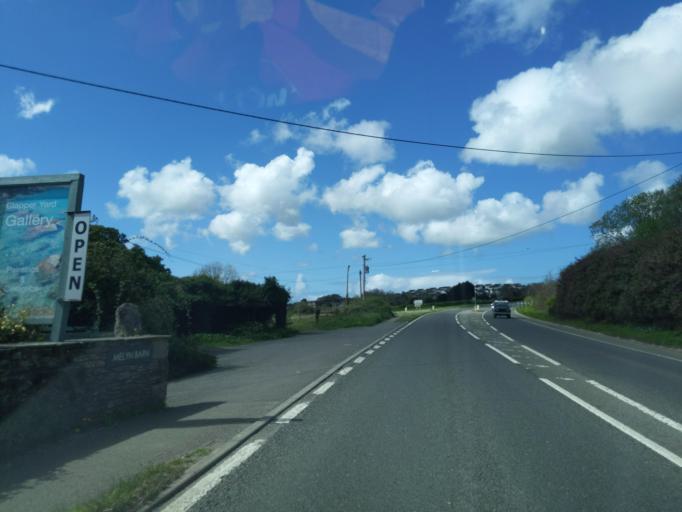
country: GB
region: England
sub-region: Cornwall
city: Wadebridge
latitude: 50.5110
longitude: -4.8154
